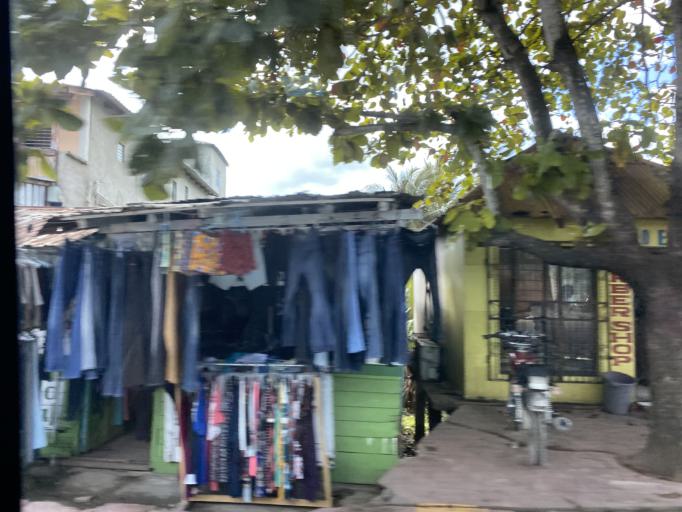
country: DO
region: Espaillat
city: Jamao al Norte
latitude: 19.6681
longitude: -70.3679
